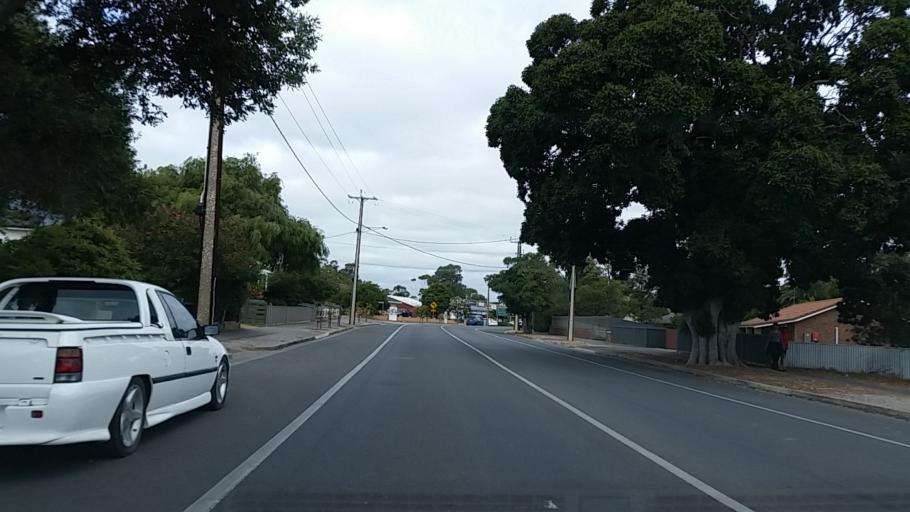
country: AU
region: South Australia
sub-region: Yankalilla
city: Normanville
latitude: -35.4454
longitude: 138.3166
